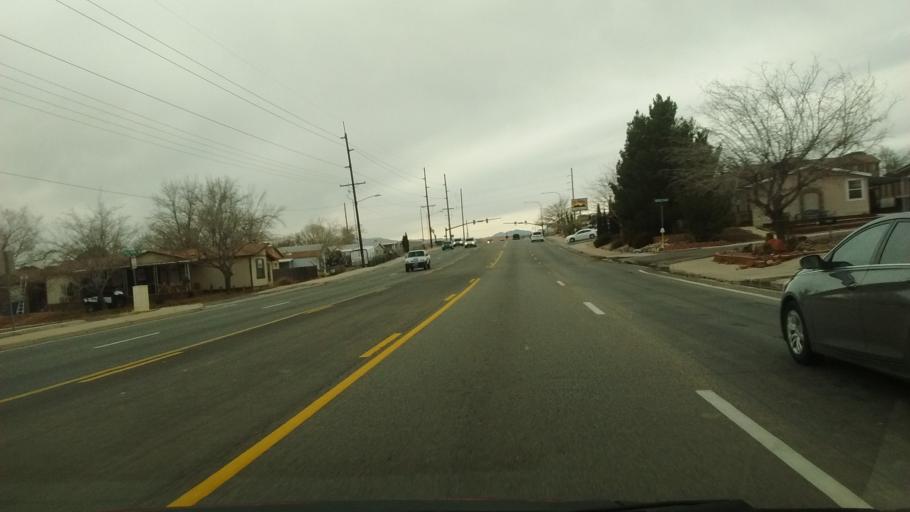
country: US
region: Utah
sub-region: Washington County
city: Washington
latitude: 37.1303
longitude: -113.5022
